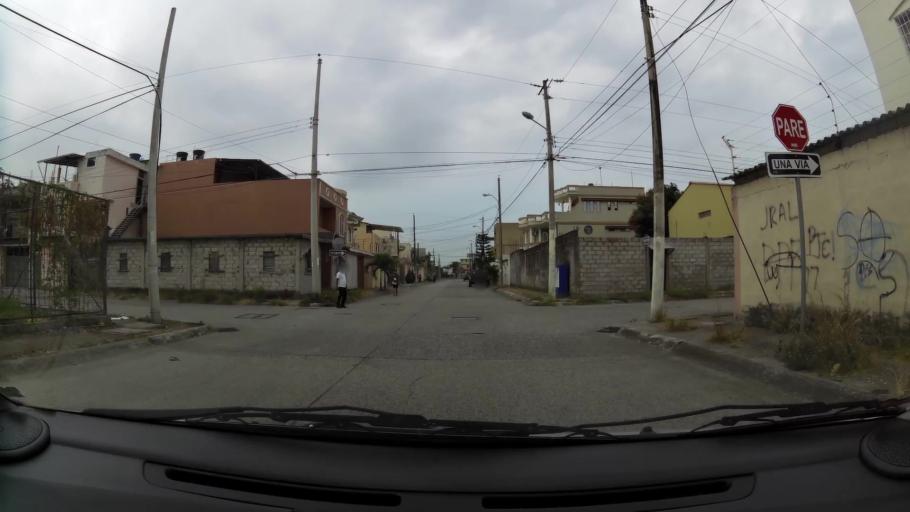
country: EC
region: Guayas
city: Eloy Alfaro
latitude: -2.1296
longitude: -79.8841
